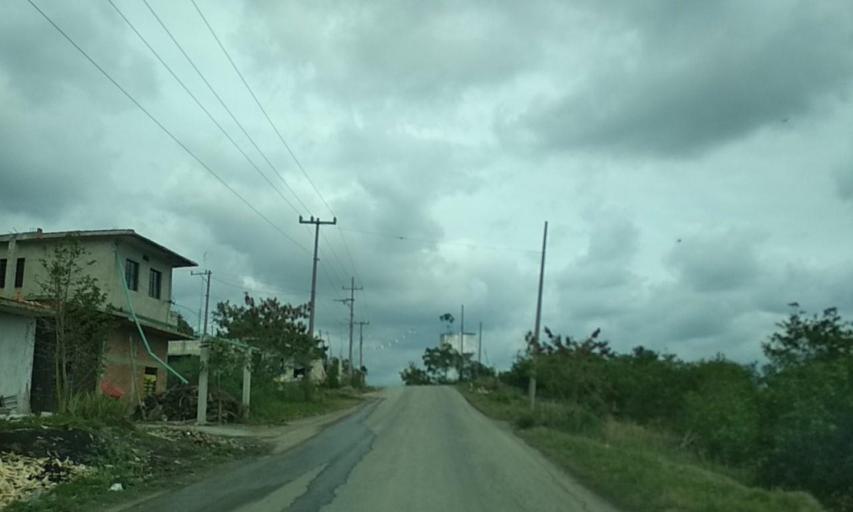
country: MX
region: Veracruz
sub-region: Papantla
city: El Chote
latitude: 20.3569
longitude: -97.3422
